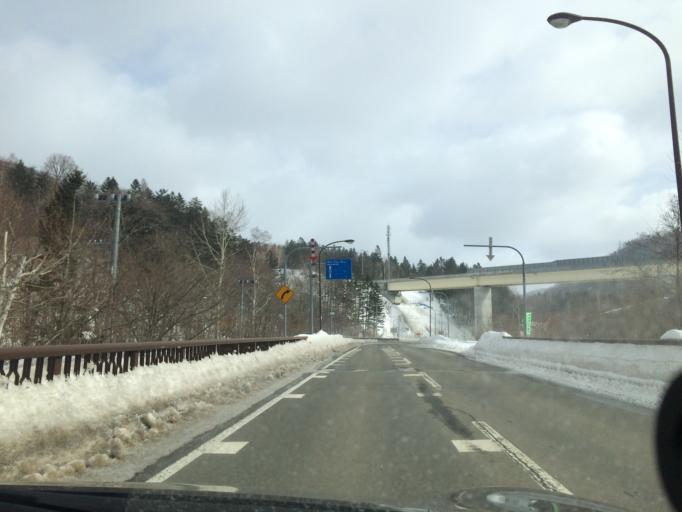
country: JP
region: Hokkaido
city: Shimo-furano
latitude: 43.0532
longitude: 142.4941
